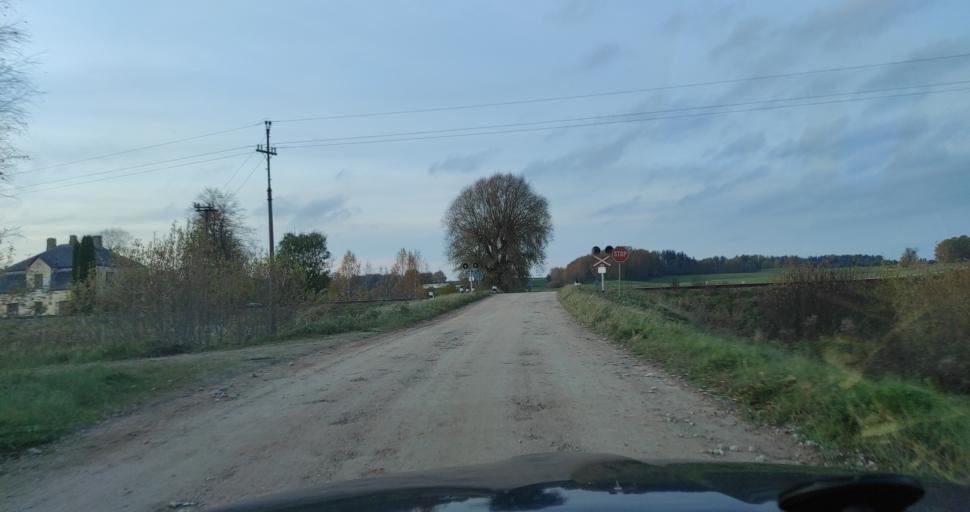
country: LV
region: Aizpute
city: Aizpute
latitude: 56.6476
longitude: 21.7961
